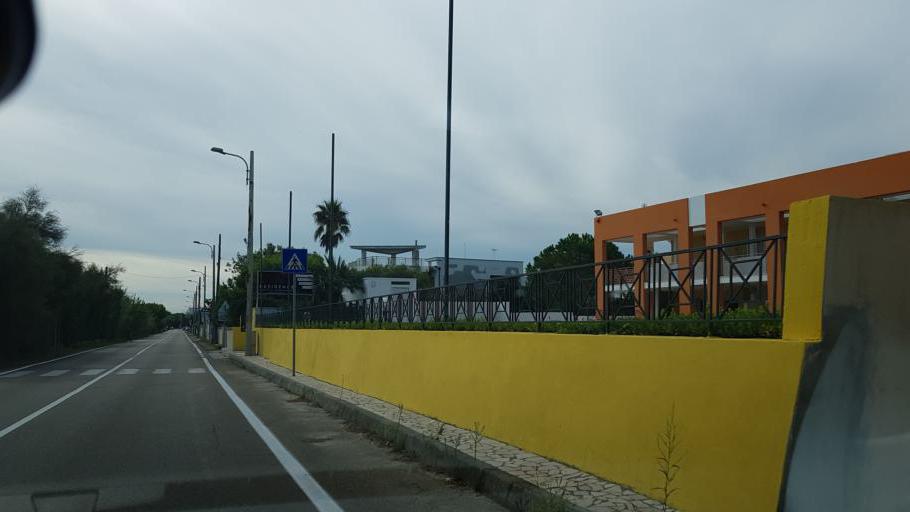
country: IT
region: Apulia
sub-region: Provincia di Lecce
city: Melendugno
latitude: 40.3272
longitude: 18.3749
